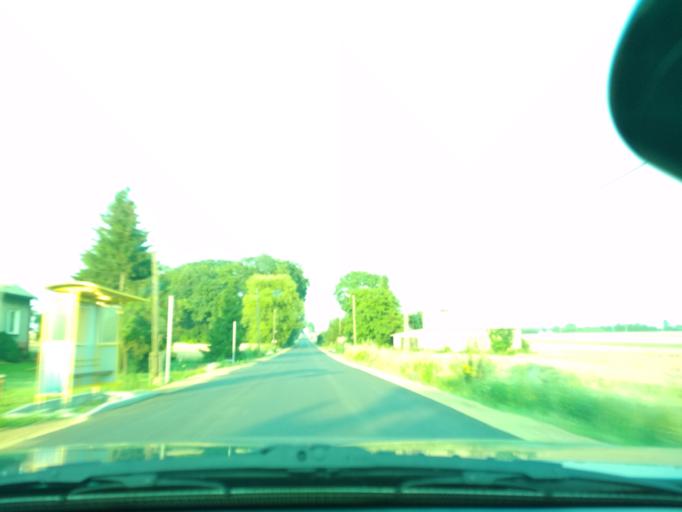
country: PL
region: Lesser Poland Voivodeship
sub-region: Powiat olkuski
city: Wolbrom
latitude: 50.4080
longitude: 19.7866
